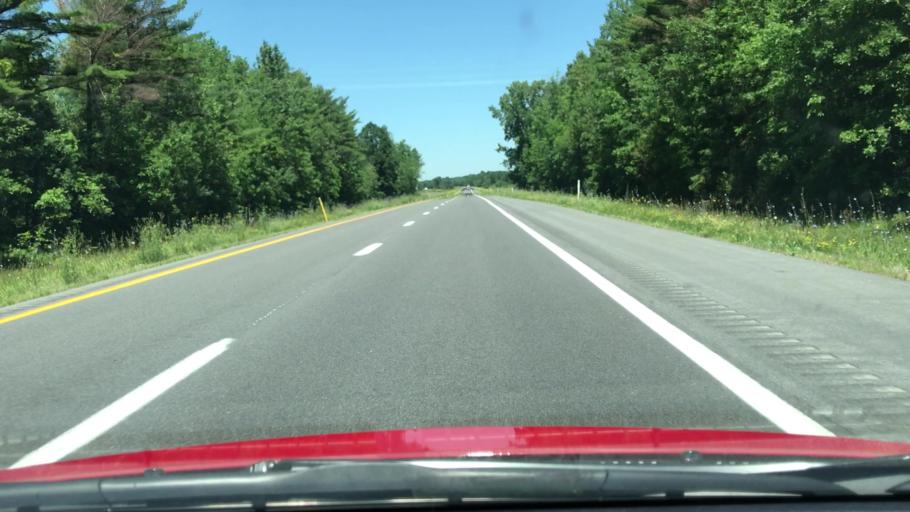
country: US
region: New York
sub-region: Clinton County
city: Cumberland Head
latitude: 44.8283
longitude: -73.4464
